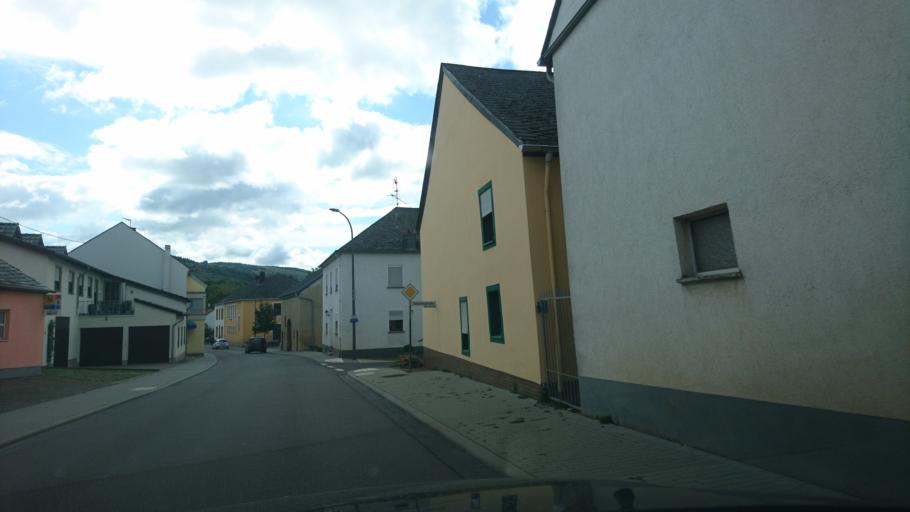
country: DE
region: Rheinland-Pfalz
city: Wiltingen
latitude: 49.6608
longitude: 6.6302
